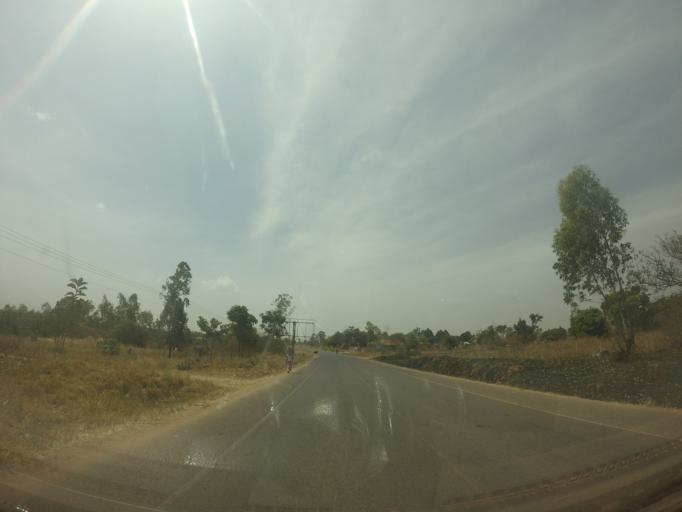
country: UG
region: Northern Region
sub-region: Arua District
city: Arua
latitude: 2.9696
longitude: 30.9189
